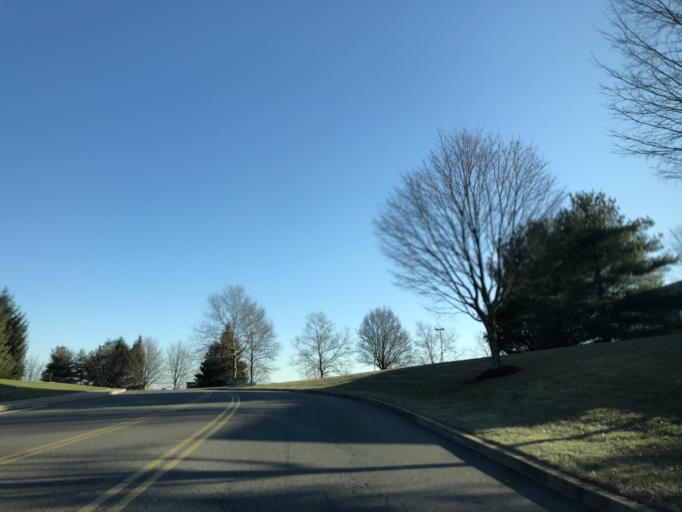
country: US
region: Pennsylvania
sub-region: Delaware County
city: Chester Heights
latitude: 39.8793
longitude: -75.5212
